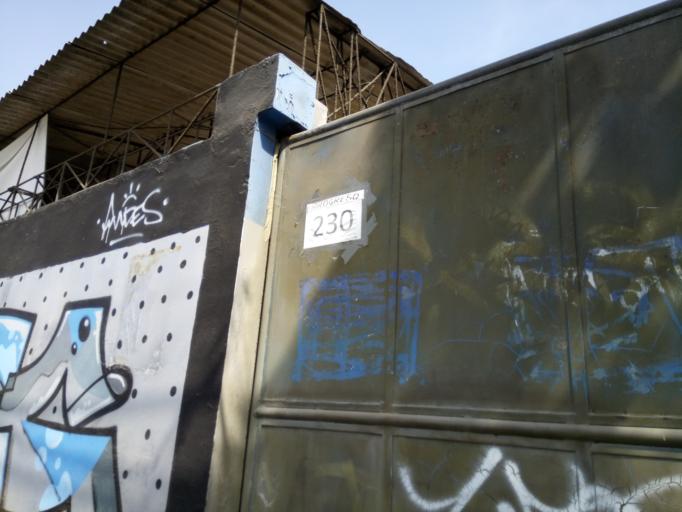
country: PE
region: Lima
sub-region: Lima
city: Surco
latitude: -12.1403
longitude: -77.0163
